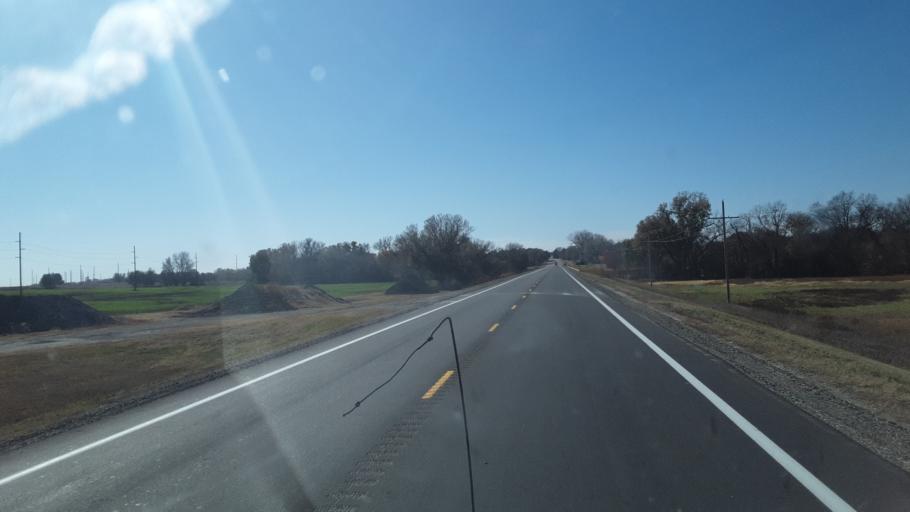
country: US
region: Kansas
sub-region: Rice County
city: Lyons
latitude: 38.3558
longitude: -98.1776
